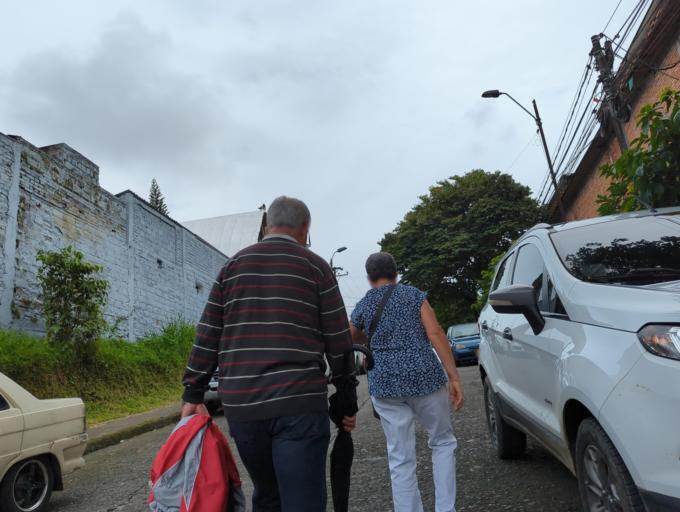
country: CO
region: Risaralda
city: Pereira
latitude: 4.8176
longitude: -75.7058
